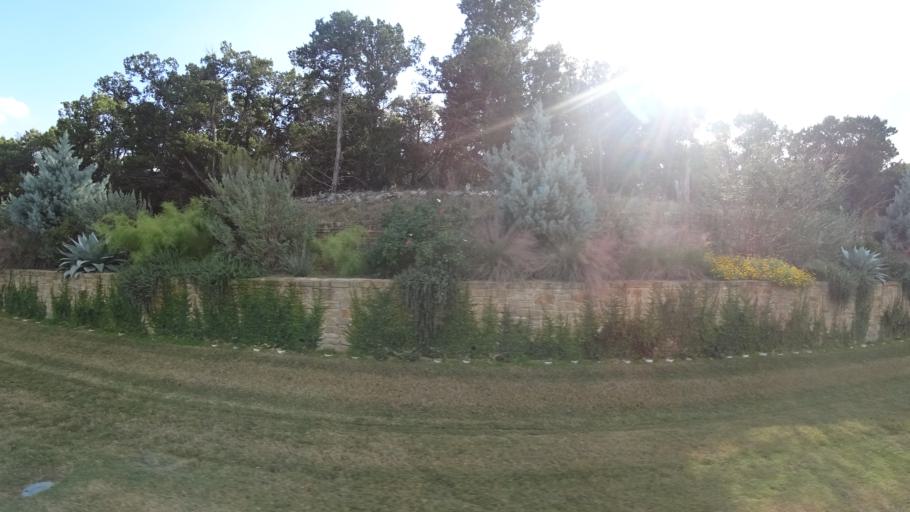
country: US
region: Texas
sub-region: Travis County
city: Barton Creek
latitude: 30.2738
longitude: -97.8812
